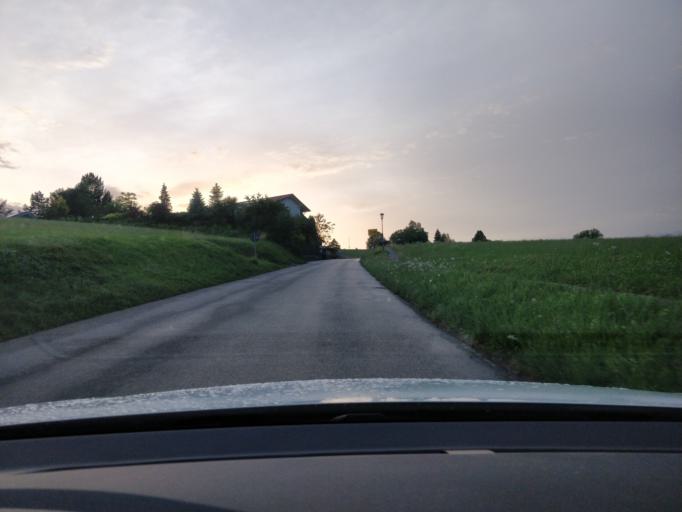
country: DE
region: Bavaria
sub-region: Upper Bavaria
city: Rimsting
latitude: 47.8744
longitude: 12.3428
